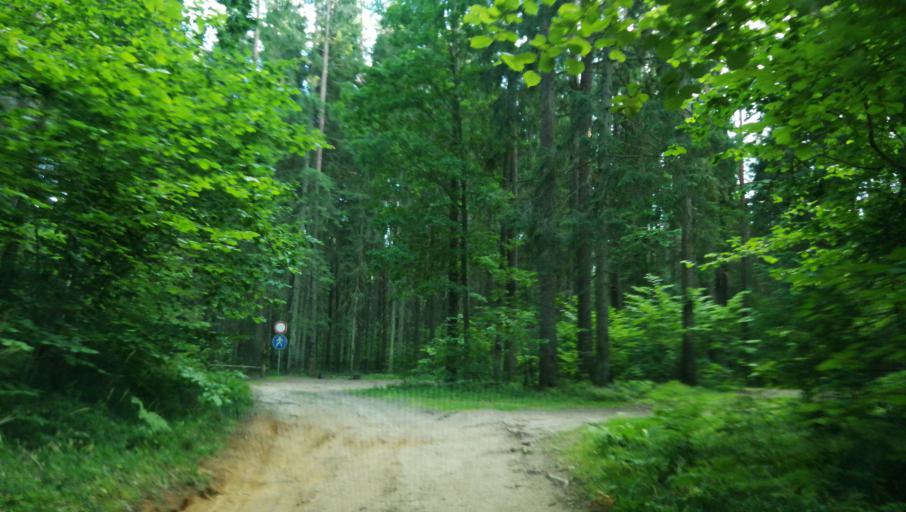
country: LV
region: Cesu Rajons
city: Cesis
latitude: 57.2822
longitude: 25.1766
